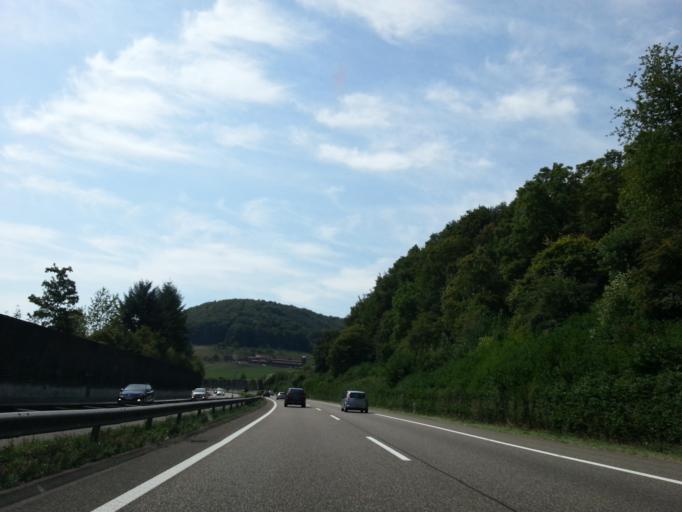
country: CH
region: Basel-Landschaft
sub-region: Bezirk Sissach
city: Zunzgen
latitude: 47.4540
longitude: 7.8022
